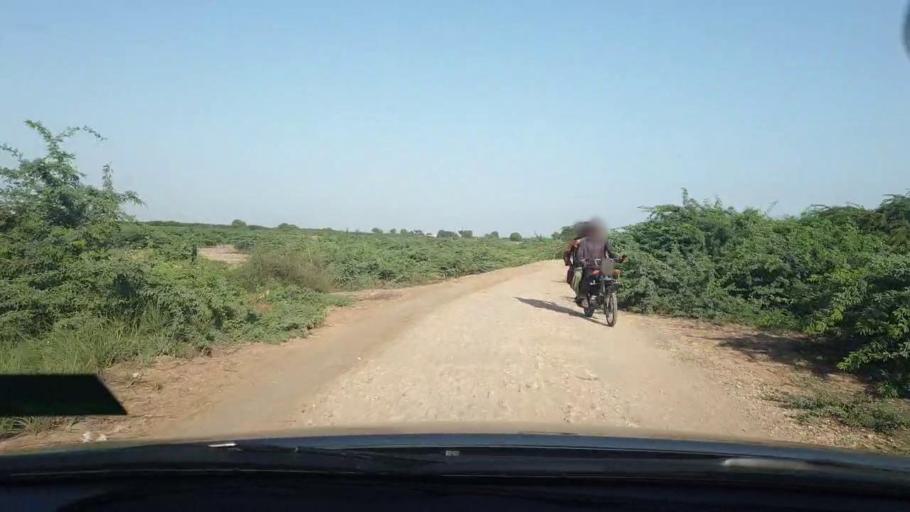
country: PK
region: Sindh
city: Naukot
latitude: 24.9149
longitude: 69.2730
